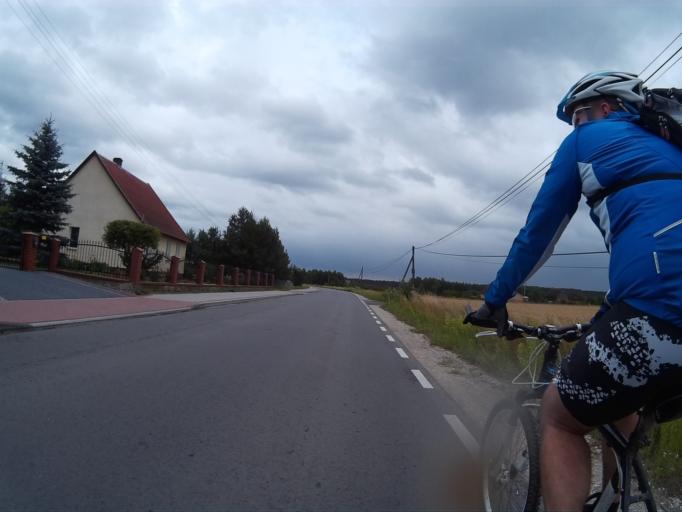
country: PL
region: Kujawsko-Pomorskie
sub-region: Powiat tucholski
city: Sliwice
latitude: 53.6340
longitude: 18.2326
